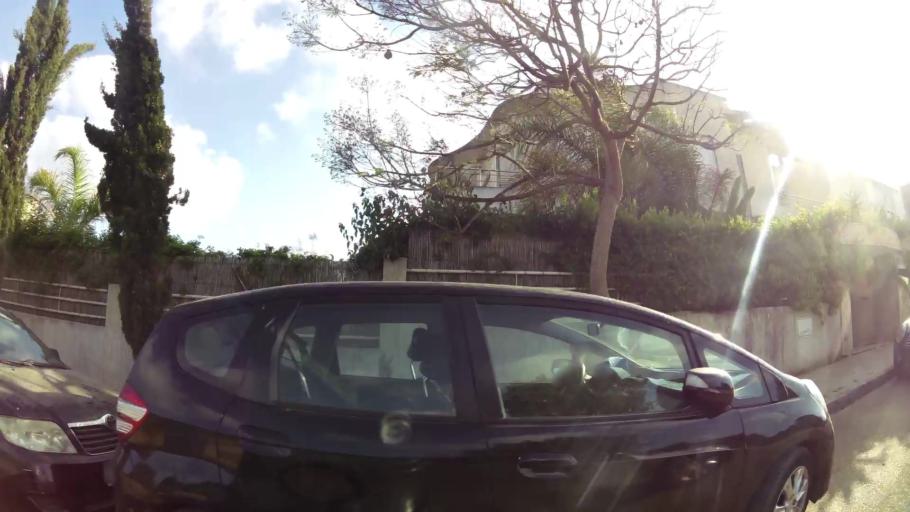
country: MA
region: Rabat-Sale-Zemmour-Zaer
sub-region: Skhirate-Temara
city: Temara
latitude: 33.9515
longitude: -6.8570
